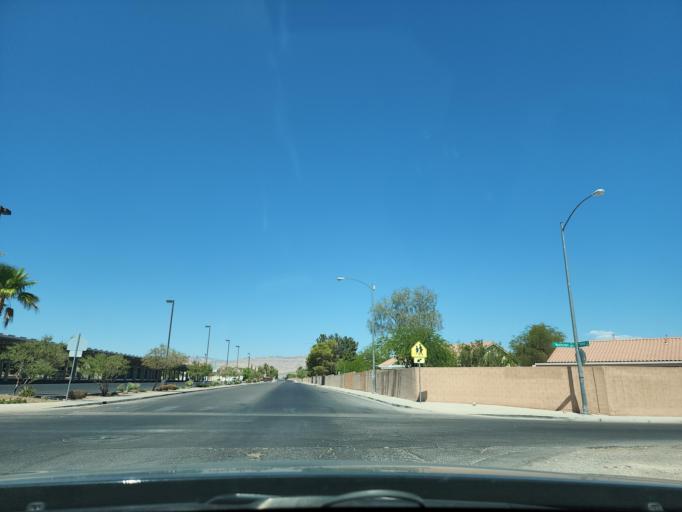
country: US
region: Nevada
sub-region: Clark County
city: Spring Valley
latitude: 36.0815
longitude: -115.2470
